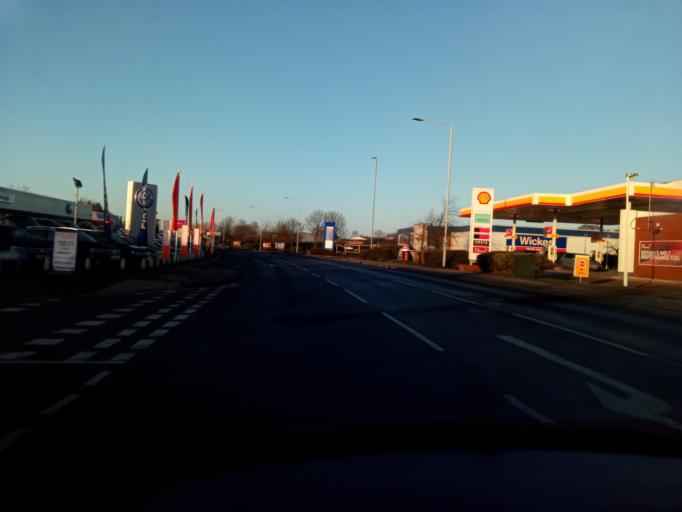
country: GB
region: England
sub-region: Leicestershire
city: Loughborough
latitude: 52.7792
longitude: -1.2113
